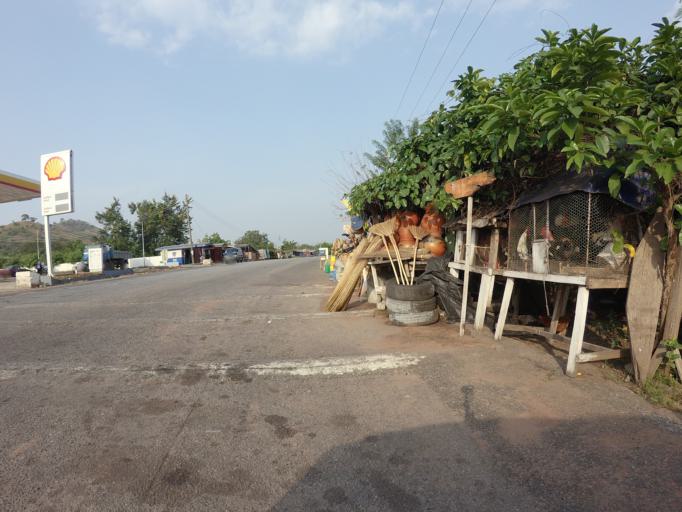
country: GH
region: Volta
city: Ho
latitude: 6.4159
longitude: 0.1735
